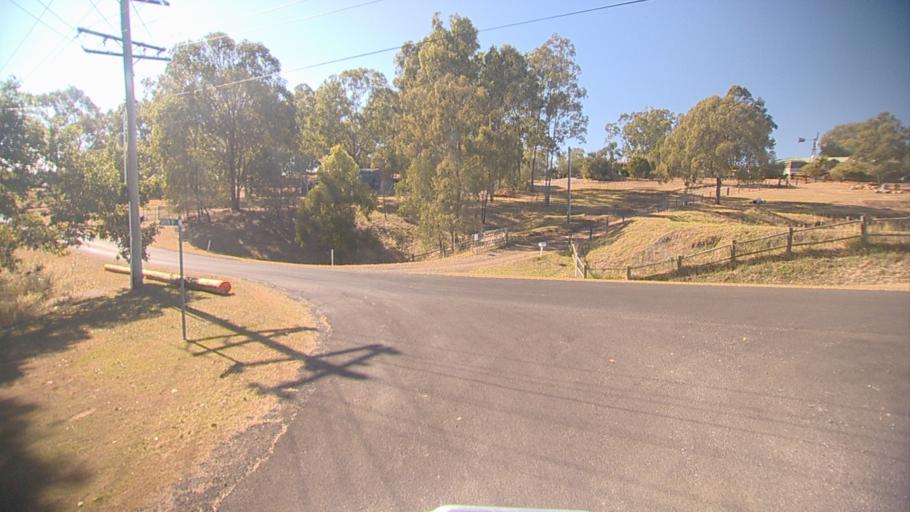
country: AU
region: Queensland
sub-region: Logan
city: Cedar Vale
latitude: -27.8907
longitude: 152.9772
